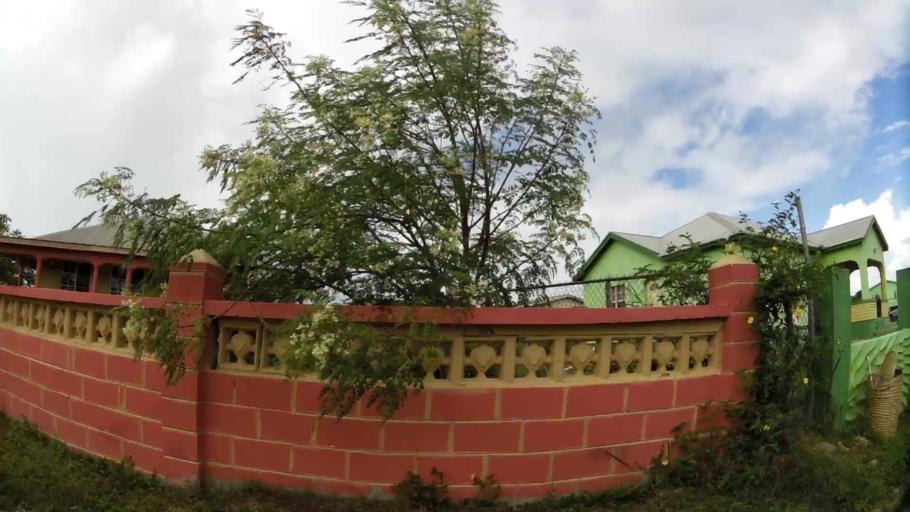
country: AG
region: Saint George
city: Piggotts
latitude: 17.1055
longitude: -61.8086
